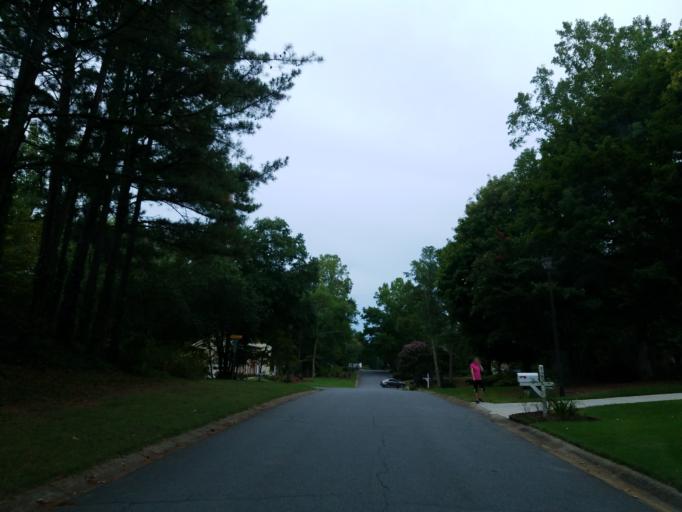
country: US
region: Georgia
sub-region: Fulton County
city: Sandy Springs
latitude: 33.9732
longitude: -84.4196
